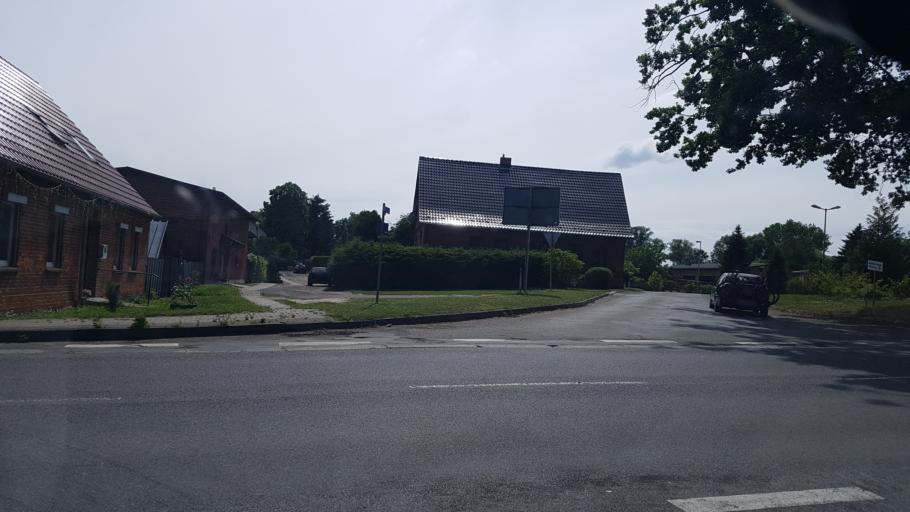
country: DE
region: Brandenburg
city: Prenzlau
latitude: 53.3224
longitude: 13.7874
